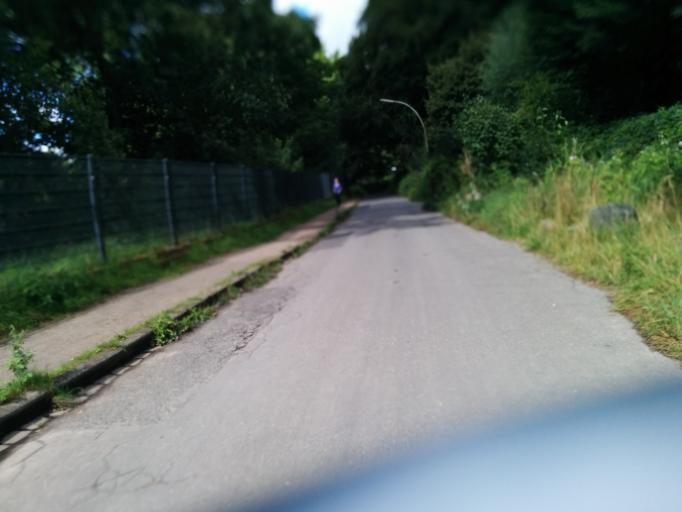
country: DE
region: Schleswig-Holstein
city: Wedel
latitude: 53.5623
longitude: 9.7794
